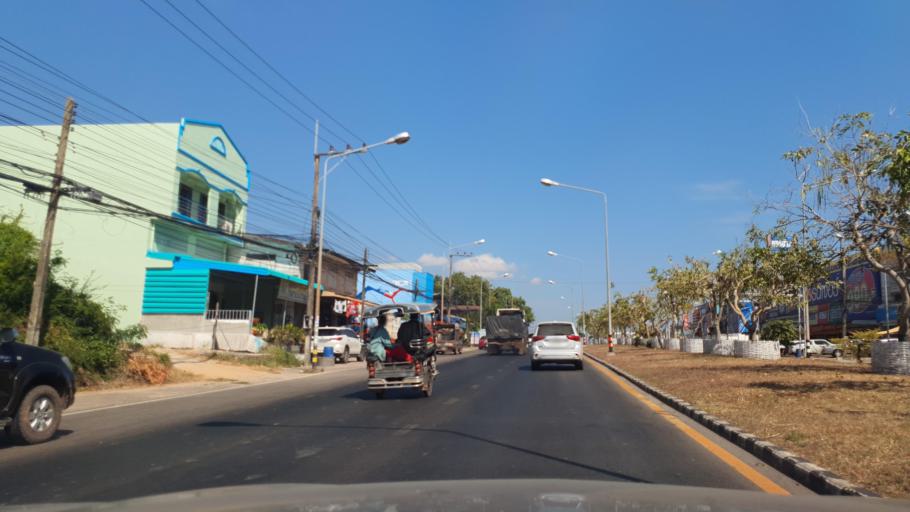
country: TH
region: Kalasin
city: Somdet
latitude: 16.6989
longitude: 103.7452
